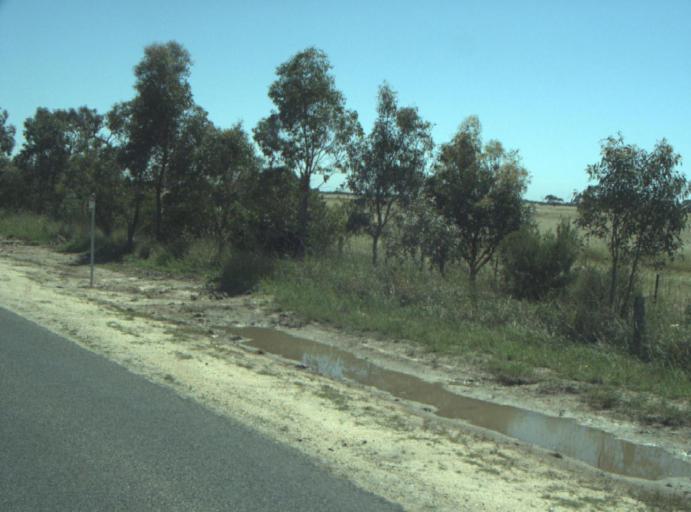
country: AU
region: Victoria
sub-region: Greater Geelong
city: Breakwater
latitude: -38.2495
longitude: 144.3510
